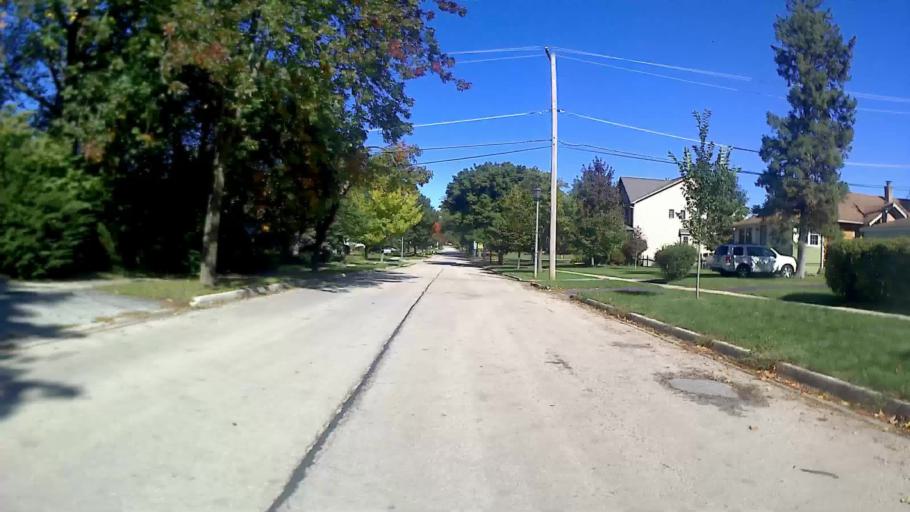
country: US
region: Illinois
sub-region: DuPage County
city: Lombard
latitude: 41.8934
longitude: -88.0255
